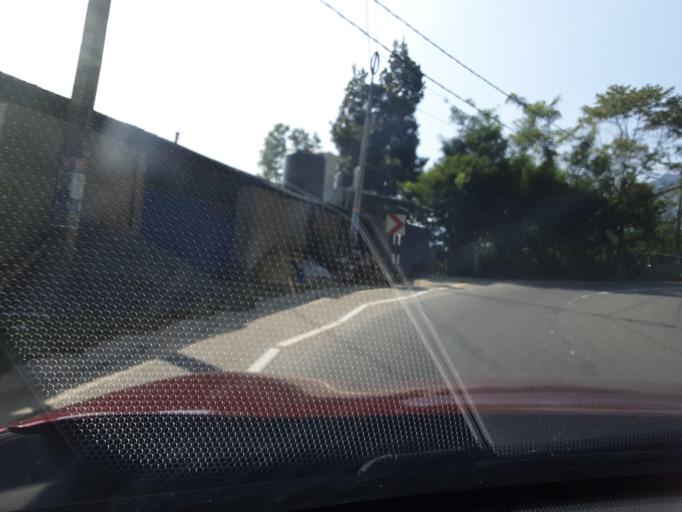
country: LK
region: Uva
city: Badulla
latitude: 6.9859
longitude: 81.0780
